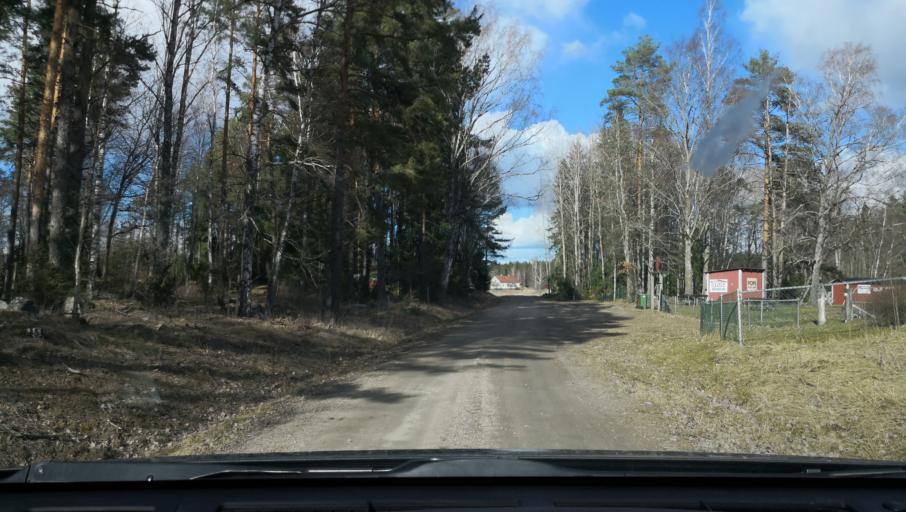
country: SE
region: OErebro
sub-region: Lindesbergs Kommun
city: Fellingsbro
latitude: 59.4312
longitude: 15.6861
